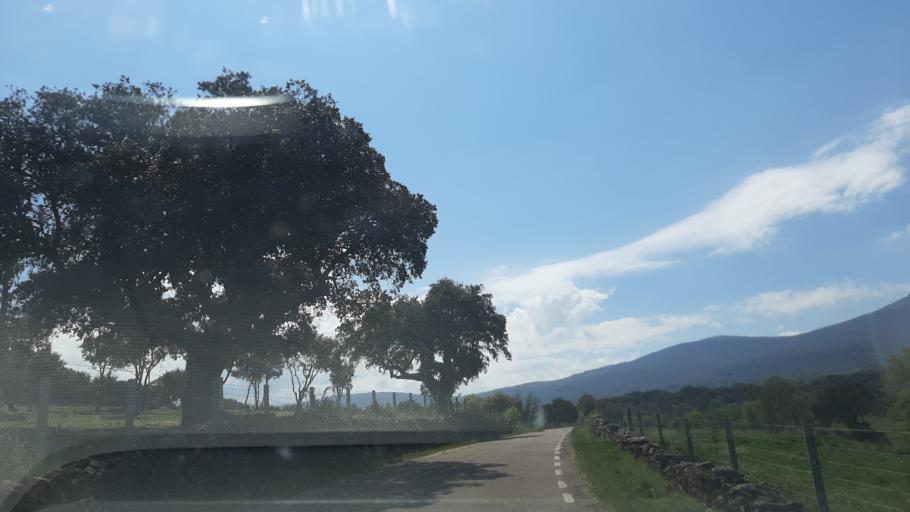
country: ES
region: Castille and Leon
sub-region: Provincia de Salamanca
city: Tejeda y Segoyuela
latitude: 40.6249
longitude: -6.0220
